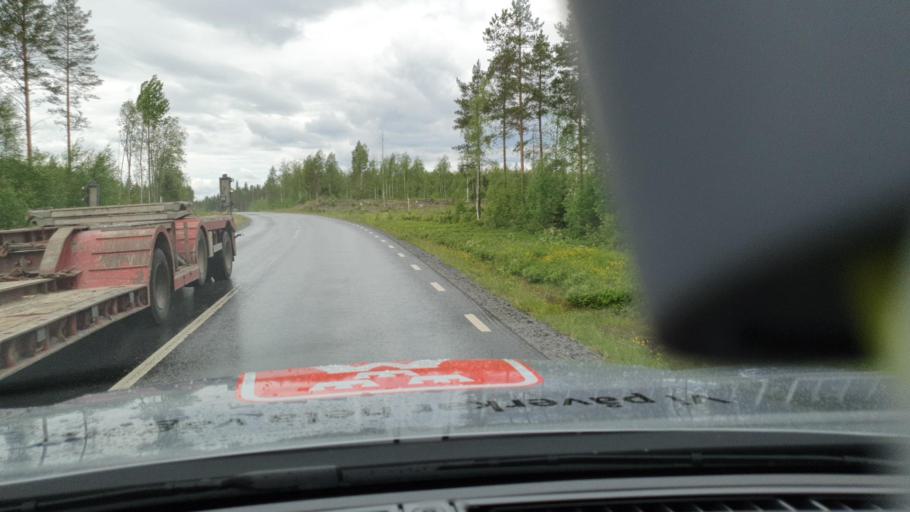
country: SE
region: Norrbotten
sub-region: Lulea Kommun
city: Ranea
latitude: 65.7896
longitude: 22.1460
